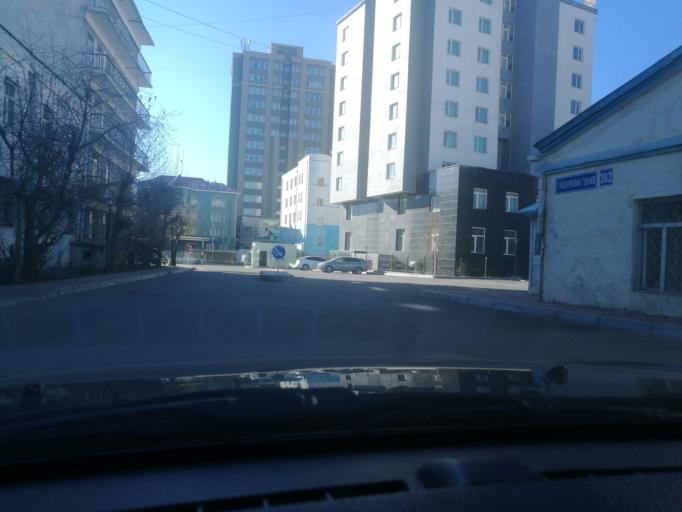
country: MN
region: Ulaanbaatar
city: Ulaanbaatar
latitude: 47.9173
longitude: 106.9271
